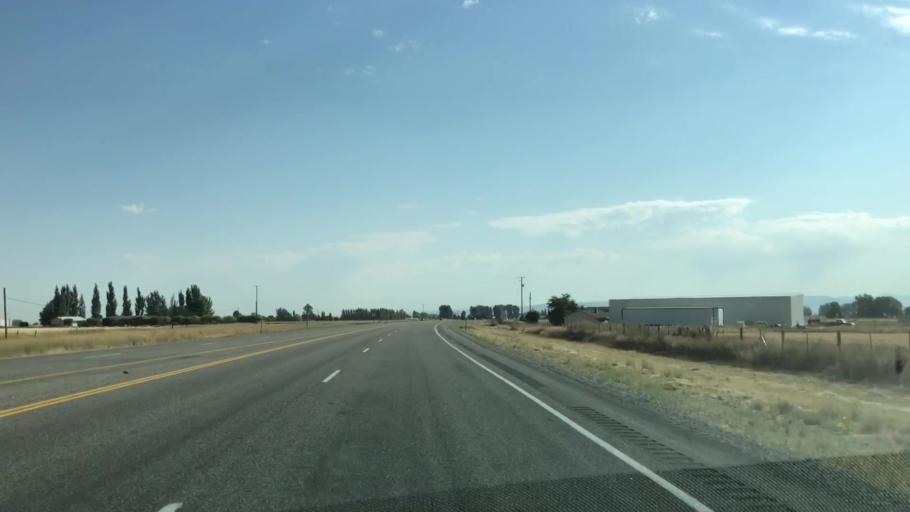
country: US
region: Idaho
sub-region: Bonneville County
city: Iona
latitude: 43.5905
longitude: -111.8812
